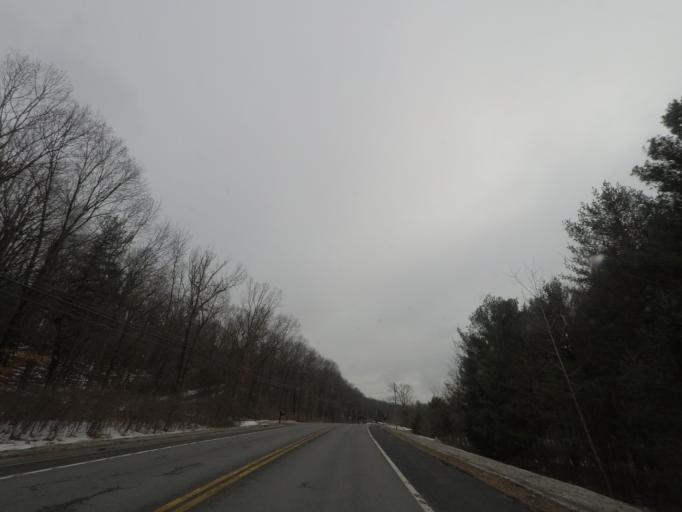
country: US
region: New York
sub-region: Albany County
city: Voorheesville
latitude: 42.6682
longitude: -73.9128
